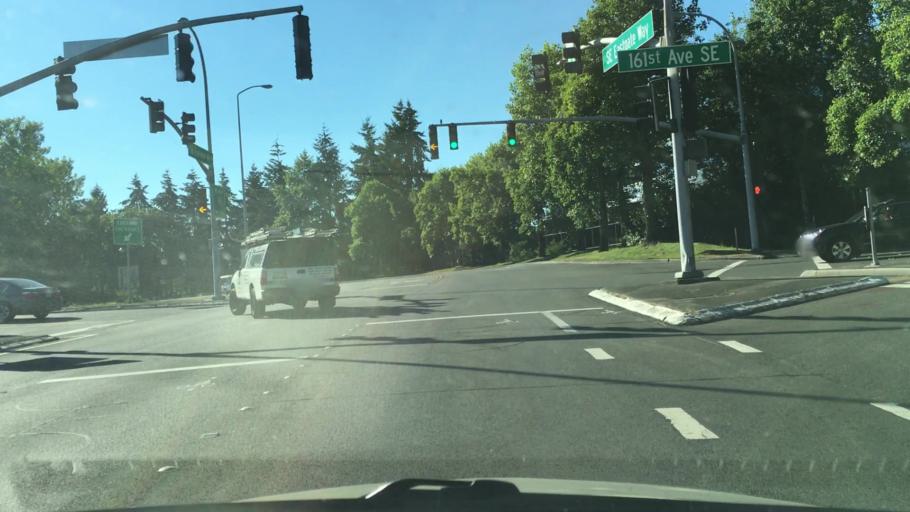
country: US
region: Washington
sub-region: King County
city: Eastgate
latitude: 47.5789
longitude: -122.1293
